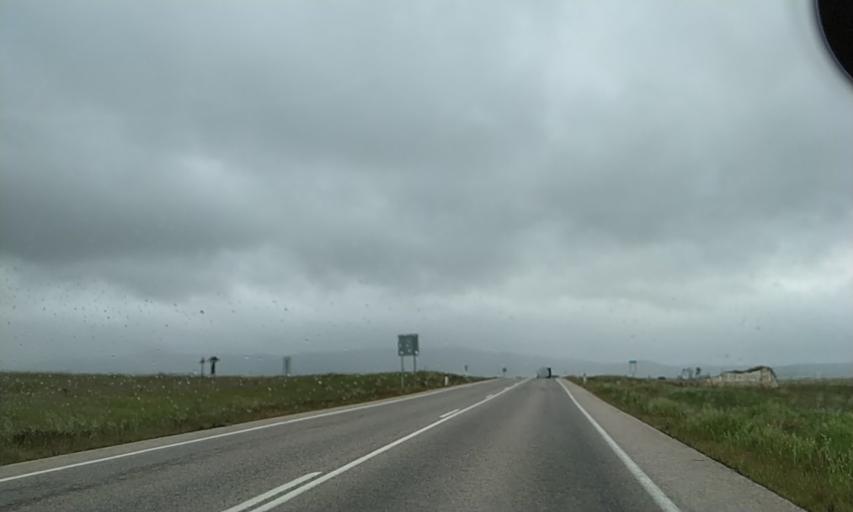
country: ES
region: Extremadura
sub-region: Provincia de Caceres
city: Malpartida de Caceres
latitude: 39.3486
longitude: -6.4709
